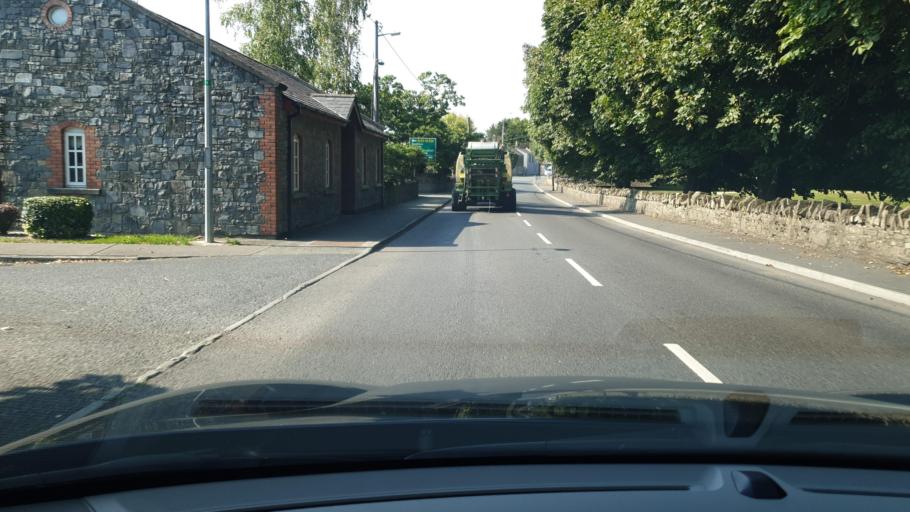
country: IE
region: Leinster
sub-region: An Mhi
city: Athboy
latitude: 53.6225
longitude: -6.9136
